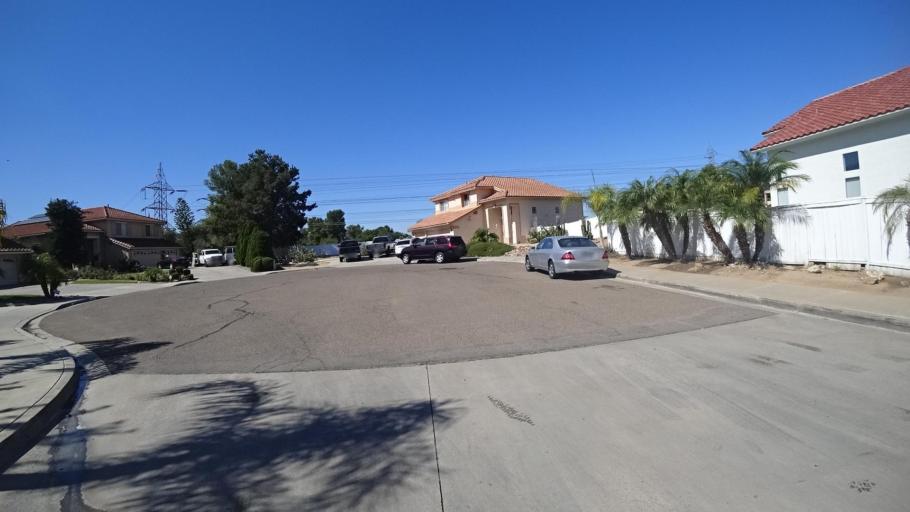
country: US
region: California
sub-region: San Diego County
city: Rancho San Diego
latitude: 32.7411
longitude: -116.9114
